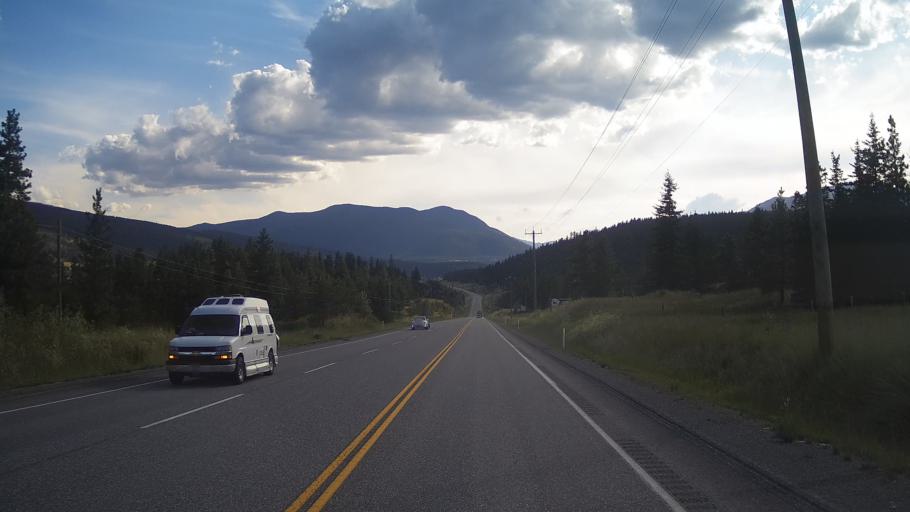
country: CA
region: British Columbia
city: Cache Creek
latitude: 51.1246
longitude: -121.5243
